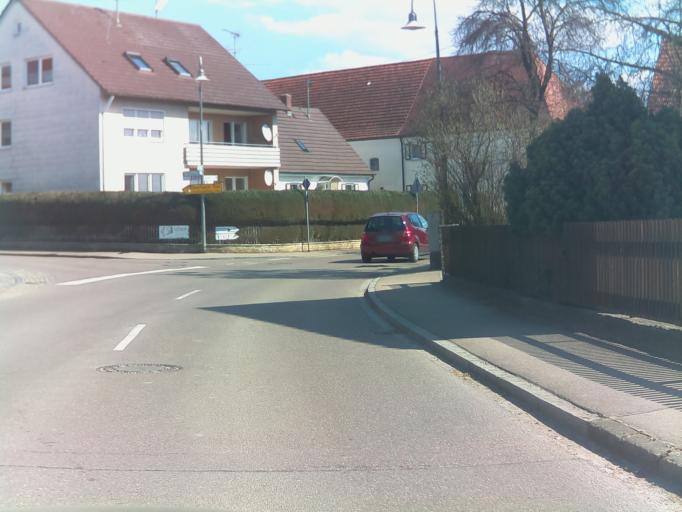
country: DE
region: Bavaria
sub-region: Swabia
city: Gablingen
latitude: 48.4818
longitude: 10.8175
